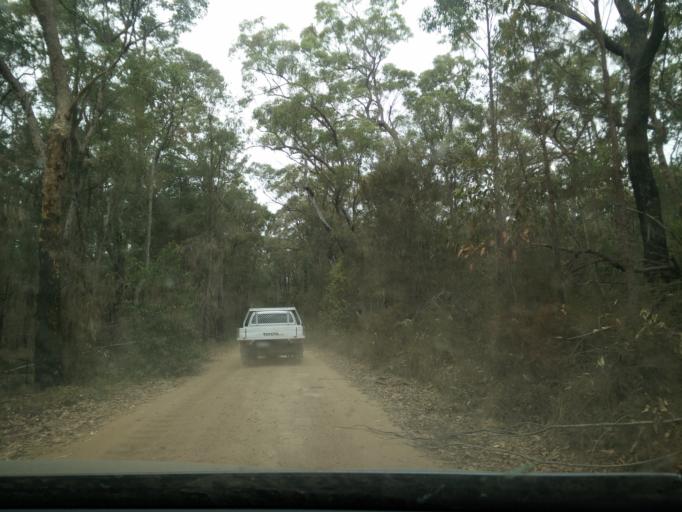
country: AU
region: New South Wales
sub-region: Blue Mountains Municipality
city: Glenbrook
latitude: -33.8260
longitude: 150.5710
